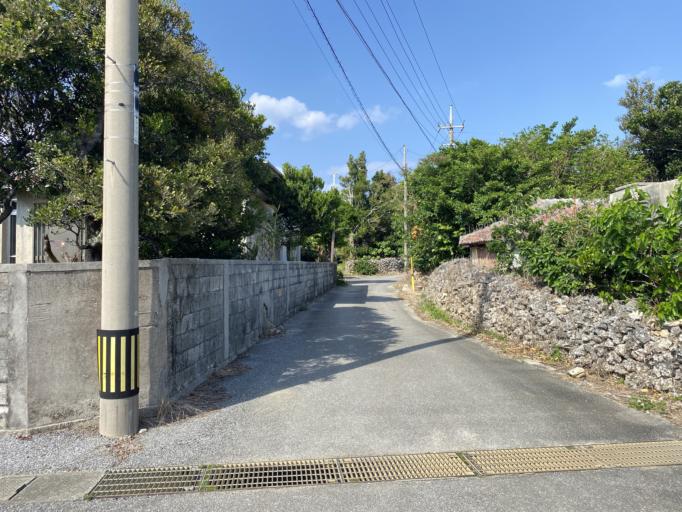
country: JP
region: Okinawa
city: Ishigaki
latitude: 24.0597
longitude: 123.7754
